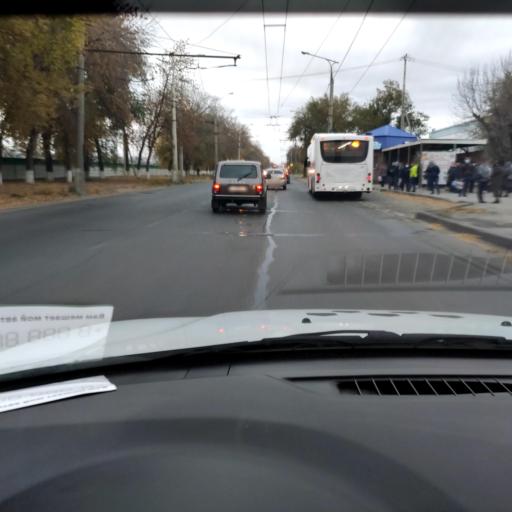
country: RU
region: Samara
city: Tol'yatti
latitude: 53.5404
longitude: 49.4431
